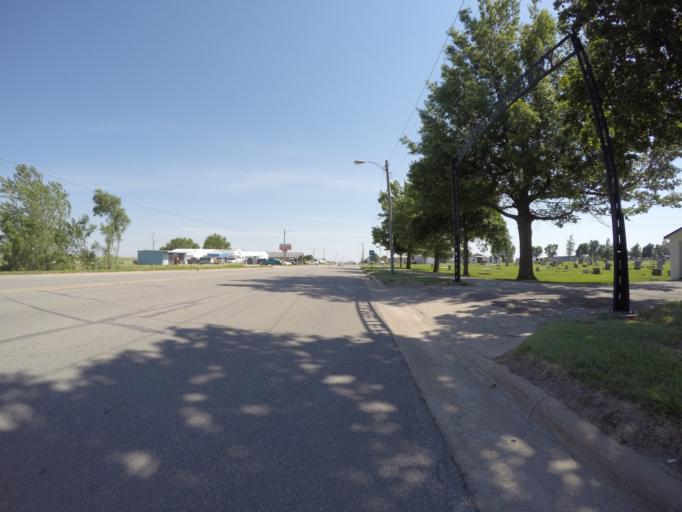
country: US
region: Kansas
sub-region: Nemaha County
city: Sabetha
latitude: 39.9012
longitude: -95.7883
